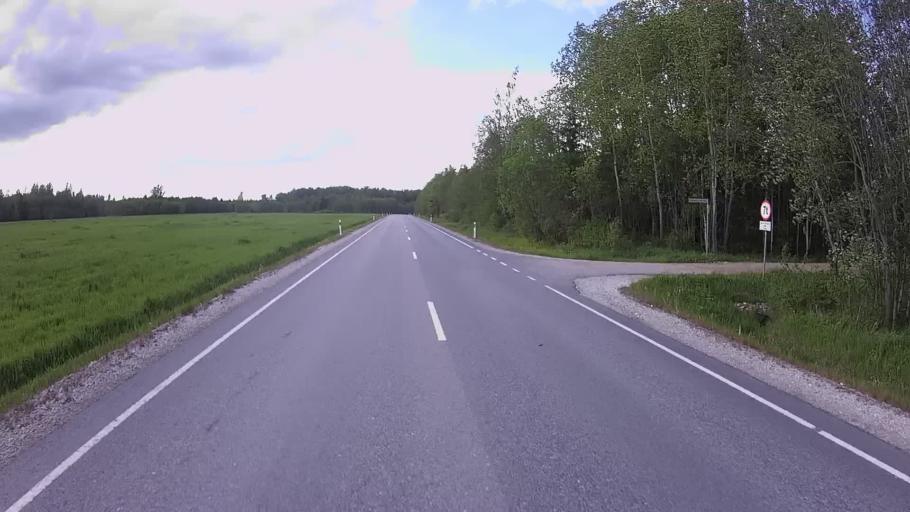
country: EE
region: Jogevamaa
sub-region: Mustvee linn
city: Mustvee
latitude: 58.8768
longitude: 26.8191
